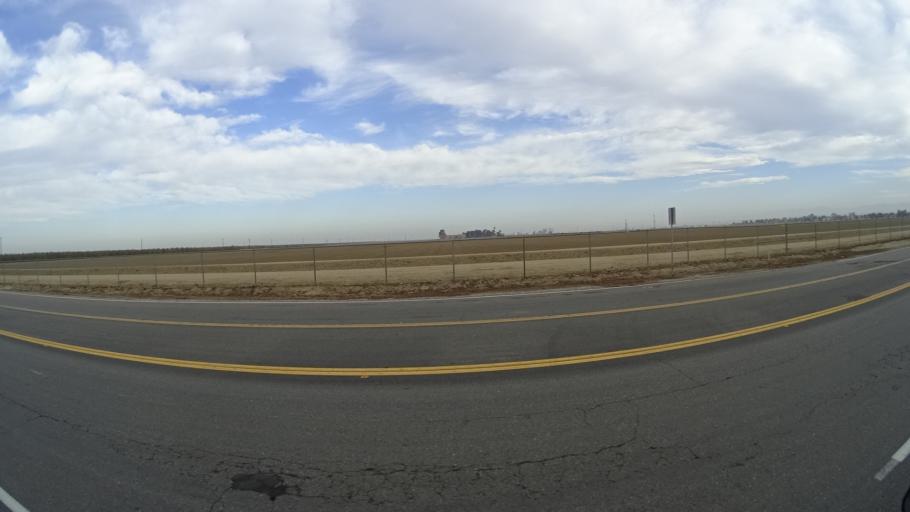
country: US
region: California
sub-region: Kern County
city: Rosedale
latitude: 35.4195
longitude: -119.1530
